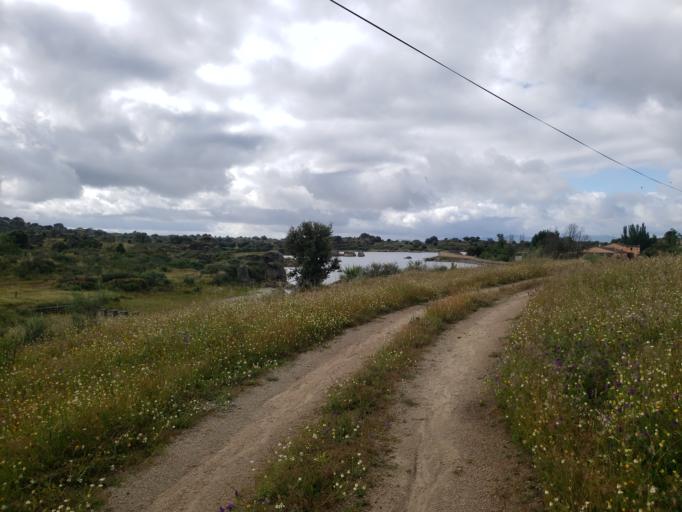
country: ES
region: Extremadura
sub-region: Provincia de Caceres
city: Malpartida de Caceres
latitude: 39.4251
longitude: -6.5042
